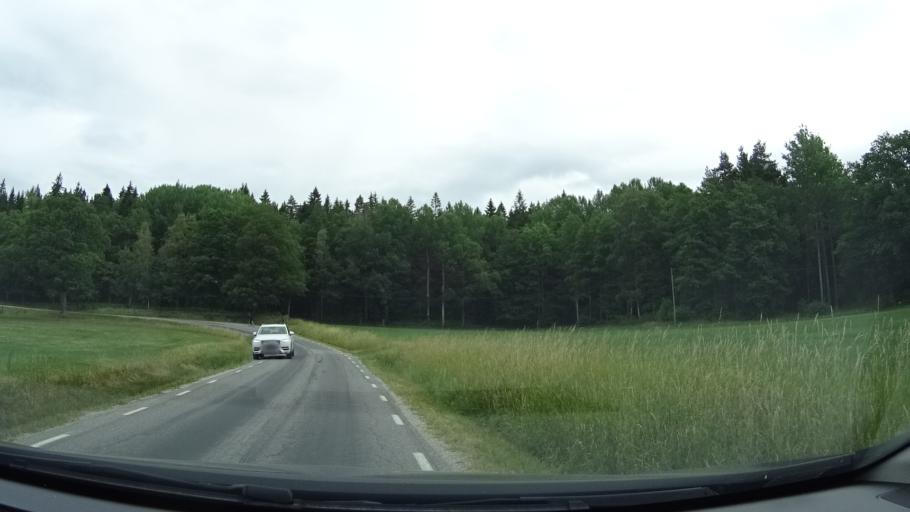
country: SE
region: Stockholm
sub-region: Varmdo Kommun
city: Mortnas
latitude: 59.3639
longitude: 18.4739
